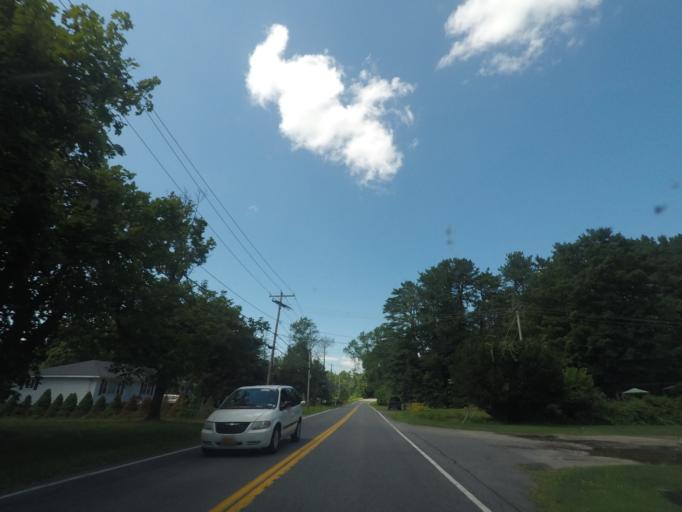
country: US
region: New York
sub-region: Schenectady County
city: Rotterdam
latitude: 42.7637
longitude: -73.9621
